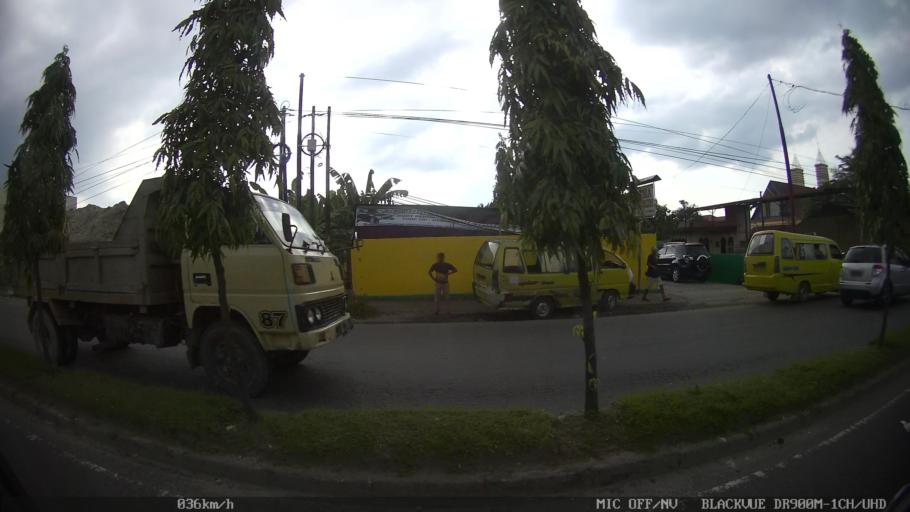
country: ID
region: North Sumatra
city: Sunggal
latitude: 3.5396
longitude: 98.6223
